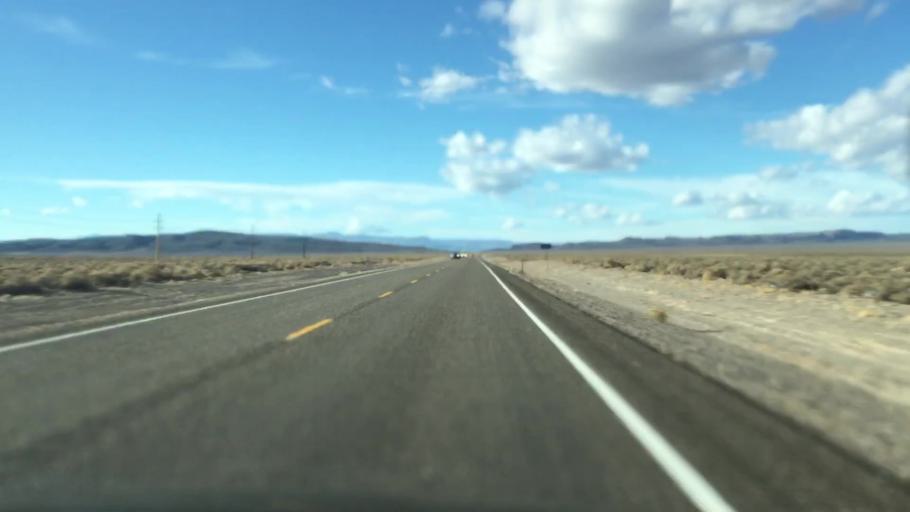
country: US
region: Nevada
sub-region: Nye County
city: Beatty
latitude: 37.1324
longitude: -116.8448
